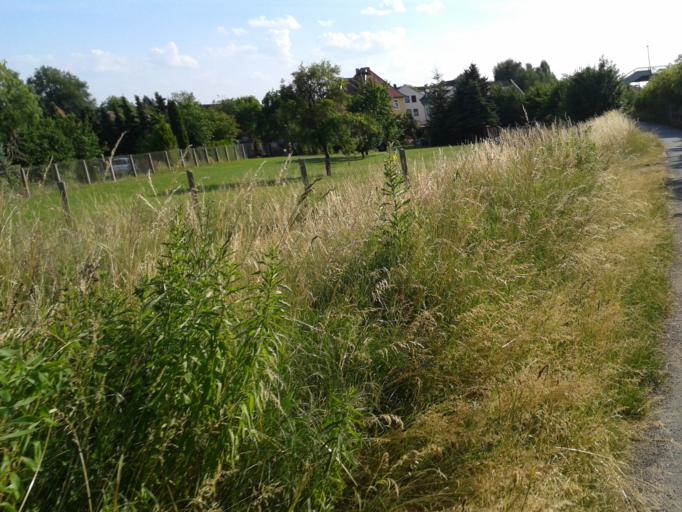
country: DE
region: Saxony
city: Albertstadt
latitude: 51.1198
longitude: 13.7621
